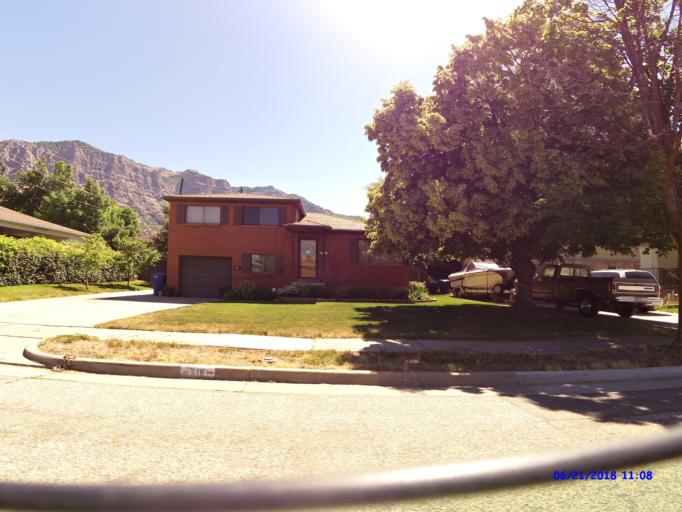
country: US
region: Utah
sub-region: Weber County
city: Ogden
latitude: 41.2548
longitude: -111.9552
